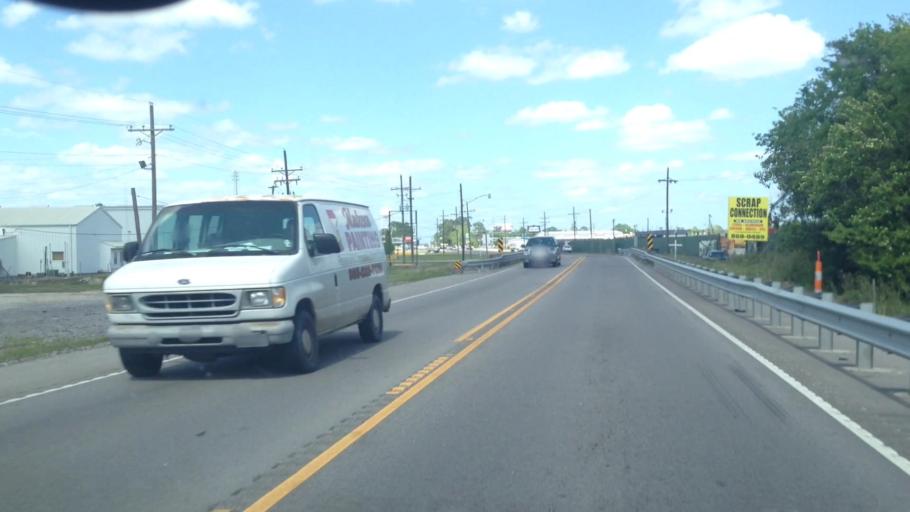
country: US
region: Louisiana
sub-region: Terrebonne Parish
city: Houma
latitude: 29.6414
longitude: -90.6914
